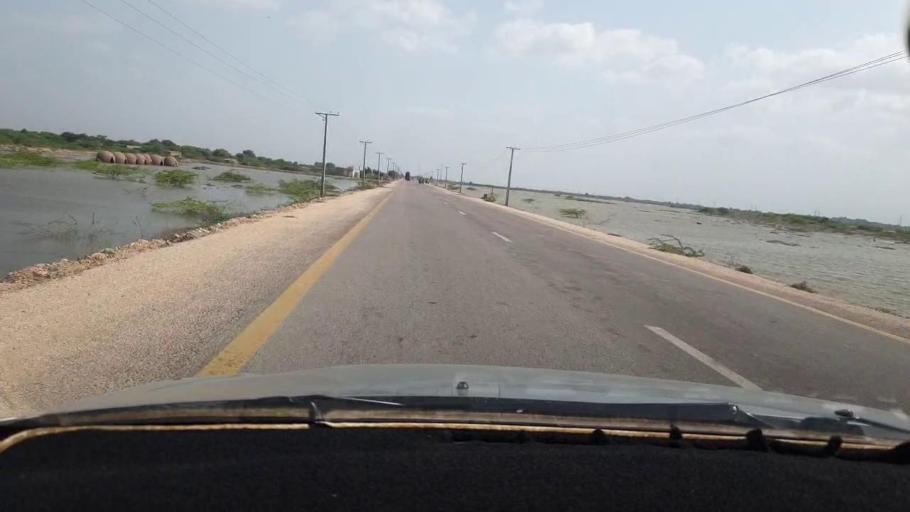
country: PK
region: Sindh
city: Naukot
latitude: 24.9312
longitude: 69.3166
